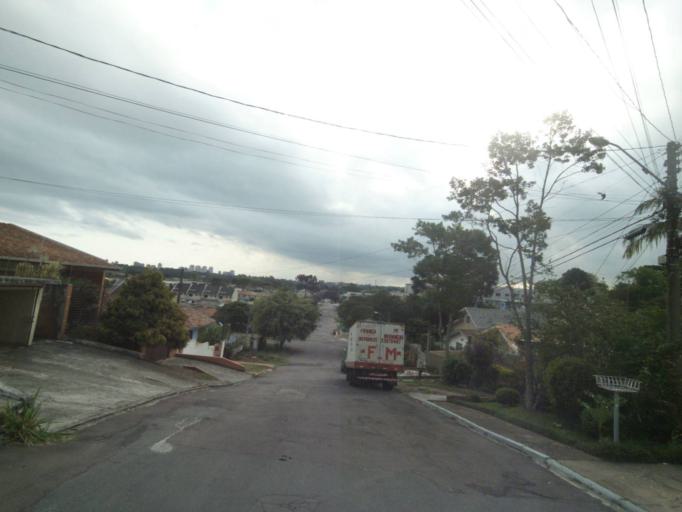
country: BR
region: Parana
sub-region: Pinhais
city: Pinhais
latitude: -25.4157
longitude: -49.2131
